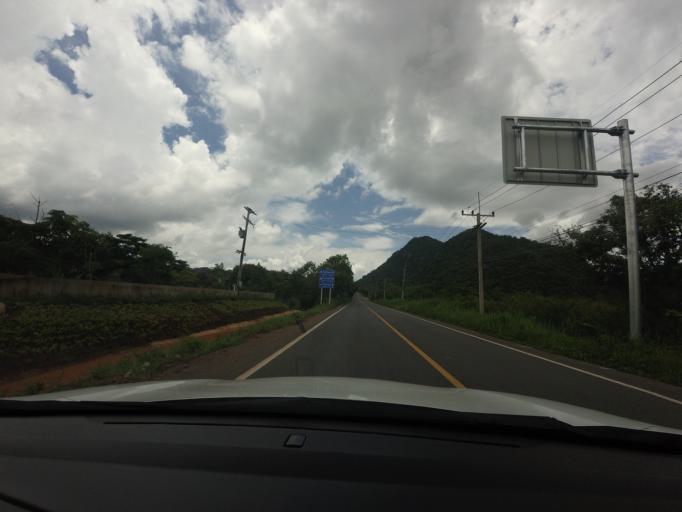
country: TH
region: Sara Buri
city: Muak Lek
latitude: 14.5517
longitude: 101.3225
